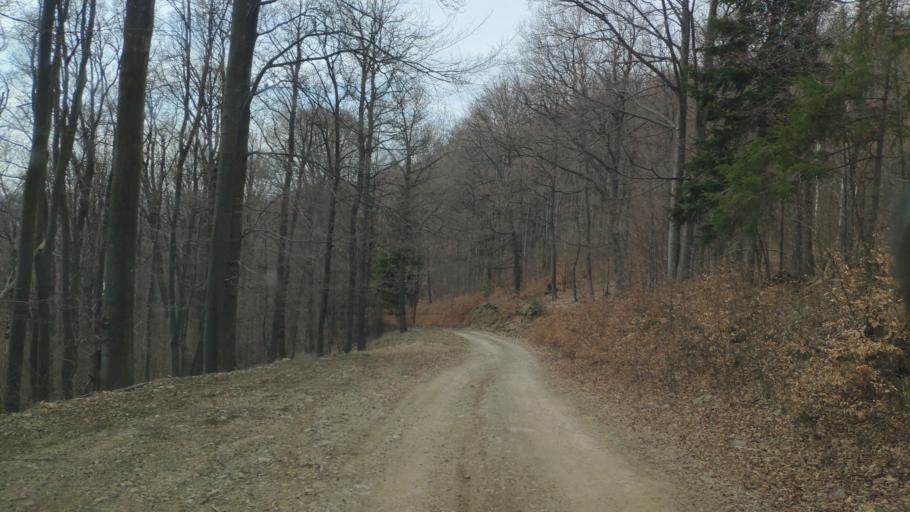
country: SK
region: Kosicky
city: Moldava nad Bodvou
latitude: 48.7414
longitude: 21.0429
